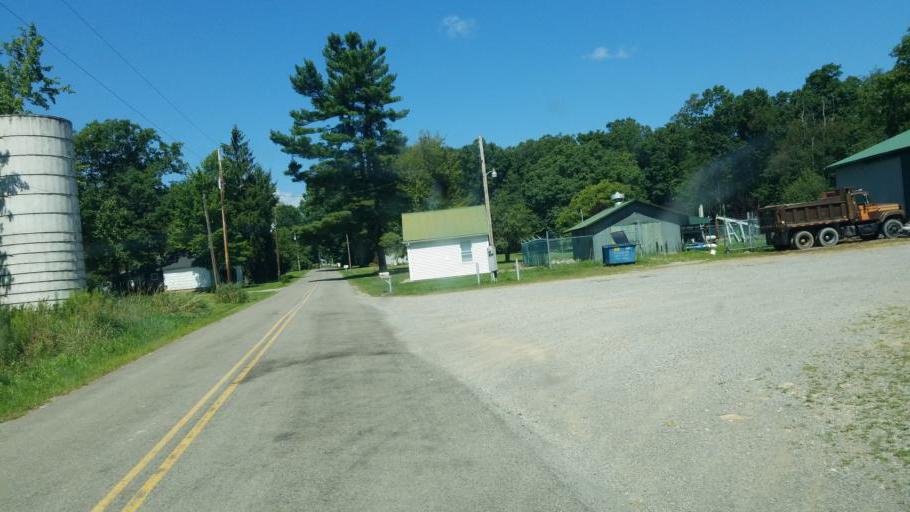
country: US
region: Pennsylvania
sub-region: Clarion County
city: Knox
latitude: 41.1911
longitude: -79.4896
